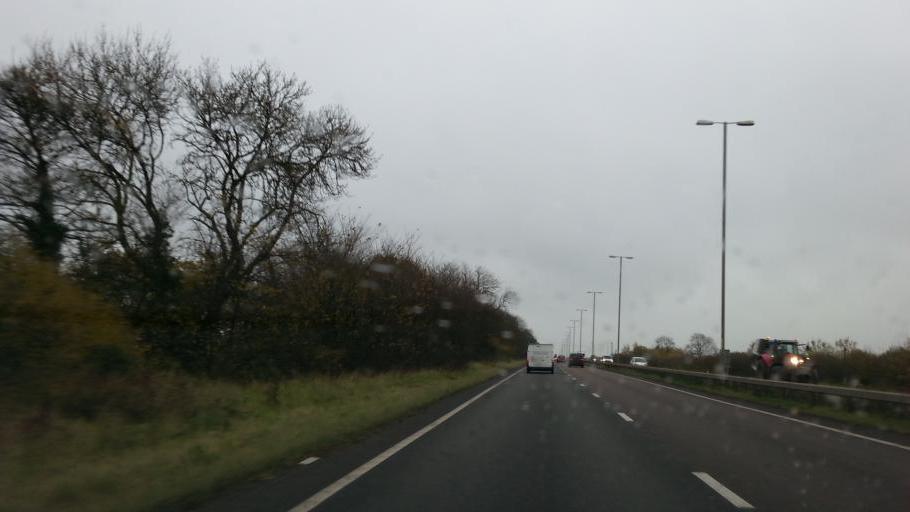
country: GB
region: England
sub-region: Lincolnshire
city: Skellingthorpe
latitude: 53.1592
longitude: -0.6647
